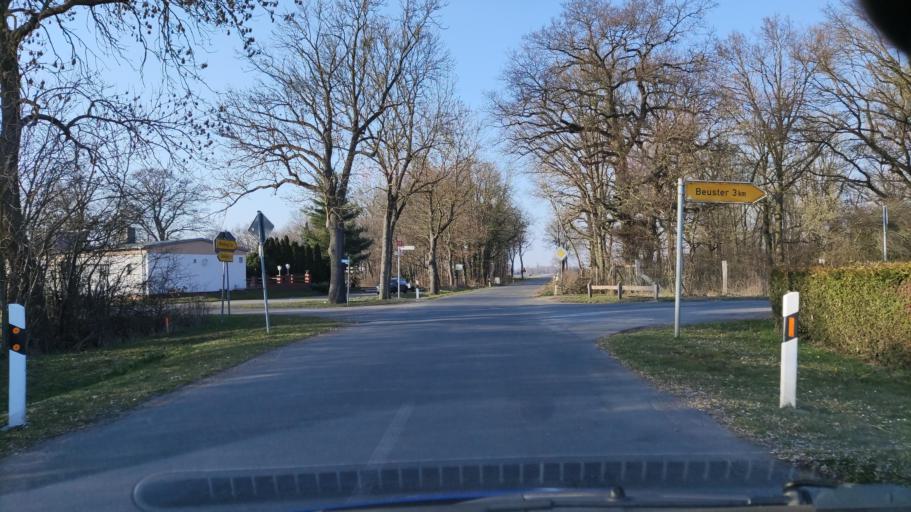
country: DE
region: Brandenburg
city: Wittenberge
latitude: 52.9540
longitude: 11.7484
